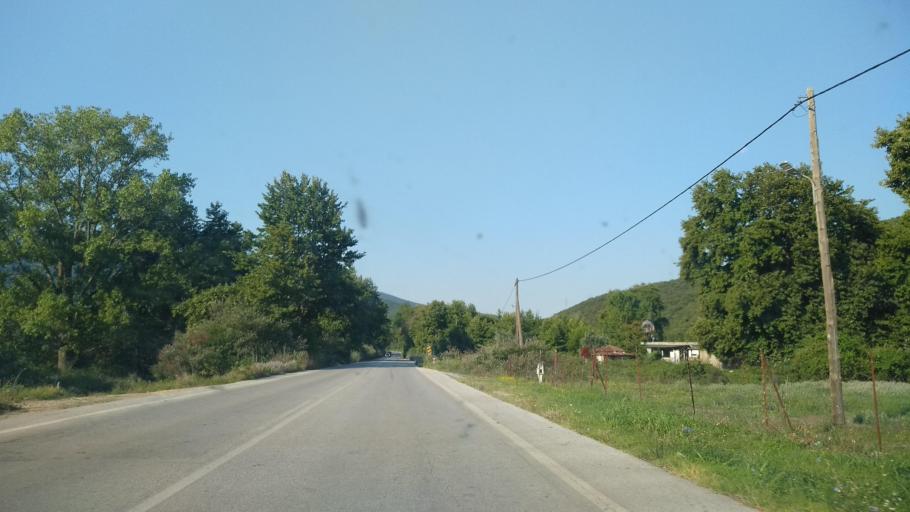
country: GR
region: Central Macedonia
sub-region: Nomos Thessalonikis
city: Stavros
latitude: 40.6846
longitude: 23.6771
